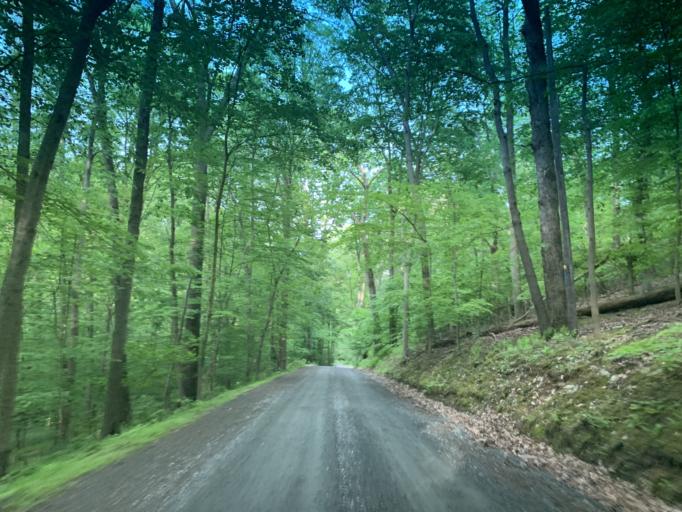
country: US
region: Pennsylvania
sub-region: York County
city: Susquehanna Trails
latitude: 39.6989
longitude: -76.2657
